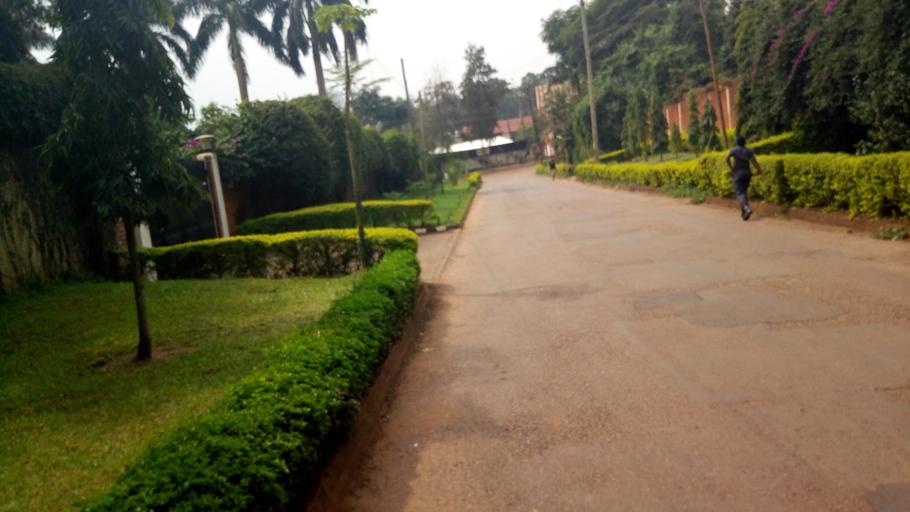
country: UG
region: Central Region
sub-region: Kampala District
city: Kampala
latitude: 0.3175
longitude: 32.6201
